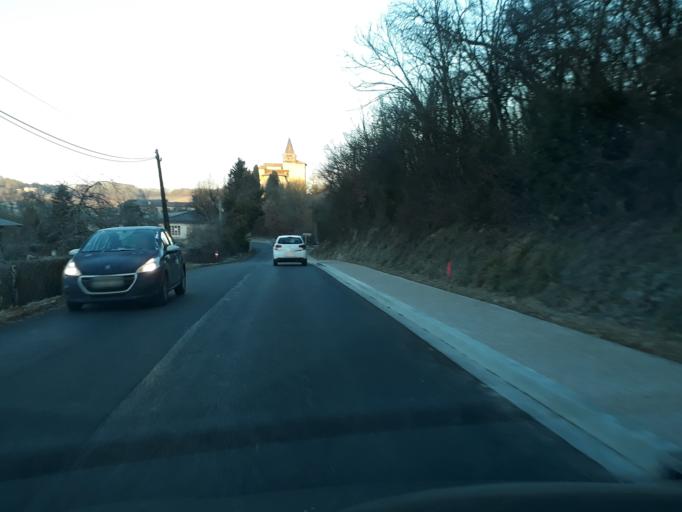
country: FR
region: Midi-Pyrenees
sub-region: Departement du Gers
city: Pavie
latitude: 43.6202
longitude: 0.6533
